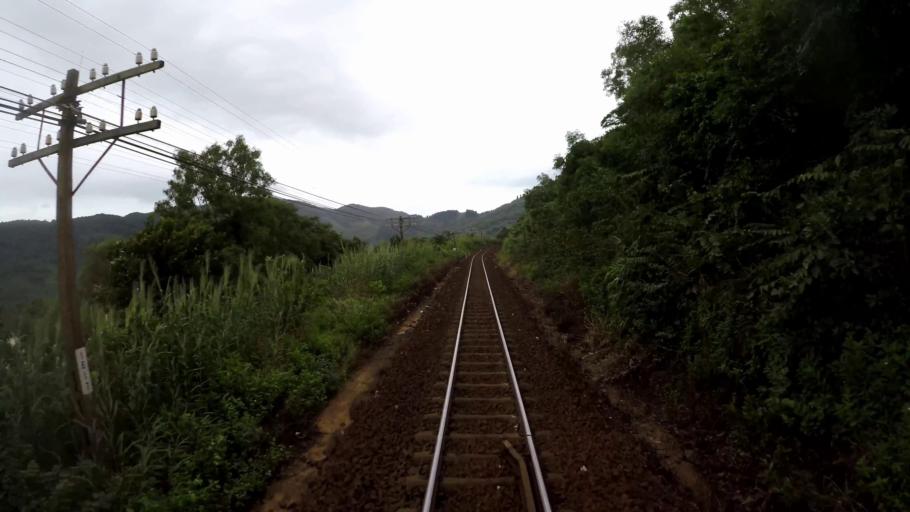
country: VN
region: Da Nang
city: Lien Chieu
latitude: 16.2128
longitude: 108.1354
